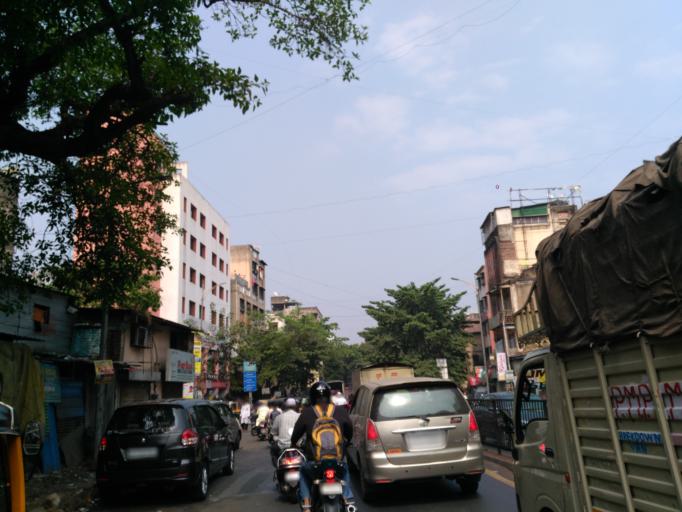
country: IN
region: Maharashtra
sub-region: Pune Division
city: Pune
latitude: 18.5173
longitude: 73.8684
